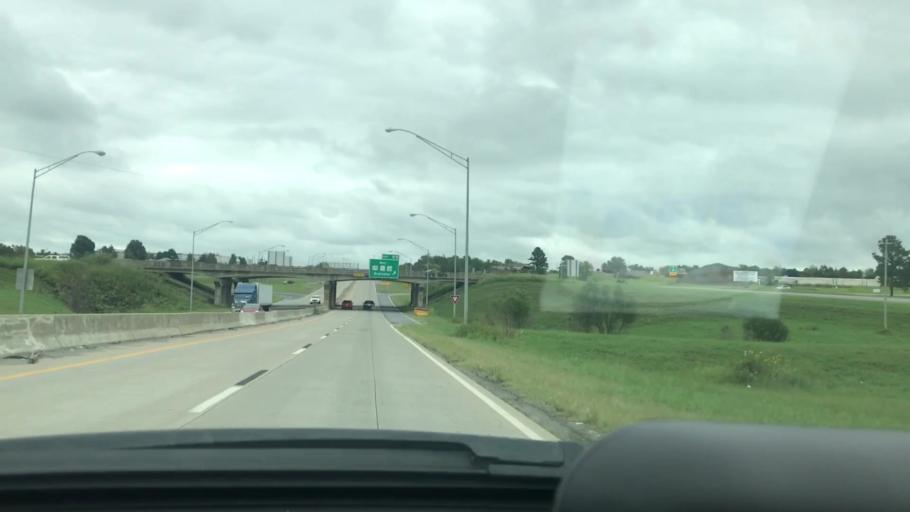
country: US
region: Oklahoma
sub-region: Pittsburg County
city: Krebs
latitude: 34.9262
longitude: -95.7411
